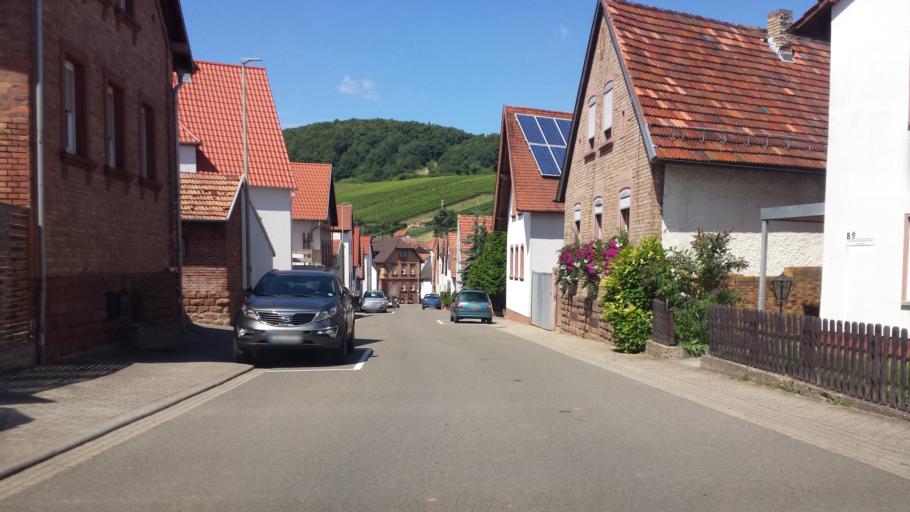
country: DE
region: Rheinland-Pfalz
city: Ranschbach
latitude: 49.1952
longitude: 8.0309
